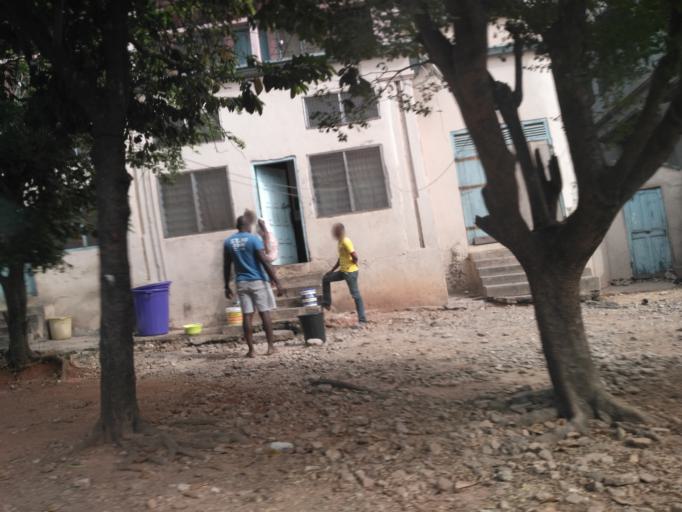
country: GH
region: Ashanti
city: Kumasi
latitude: 6.6981
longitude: -1.6111
